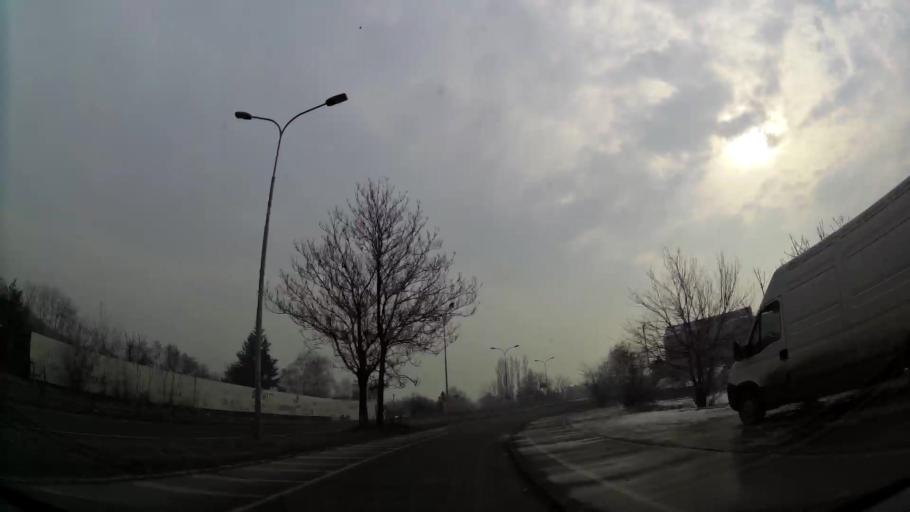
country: MK
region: Cair
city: Cair
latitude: 42.0045
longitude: 21.4696
